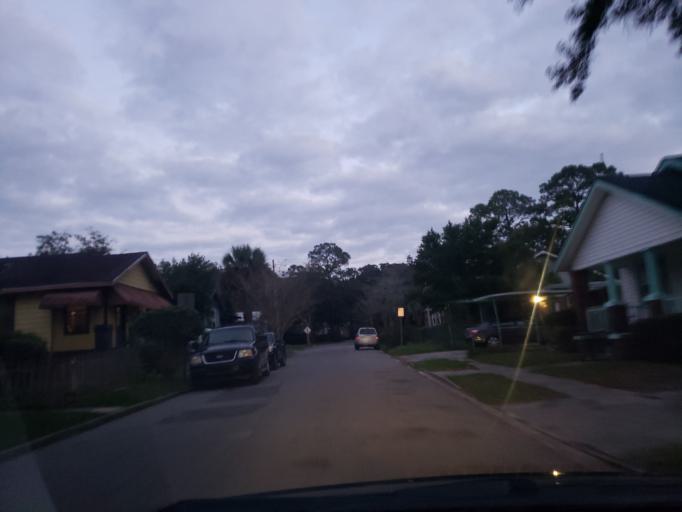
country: US
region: Georgia
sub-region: Chatham County
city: Thunderbolt
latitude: 32.0497
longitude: -81.0814
